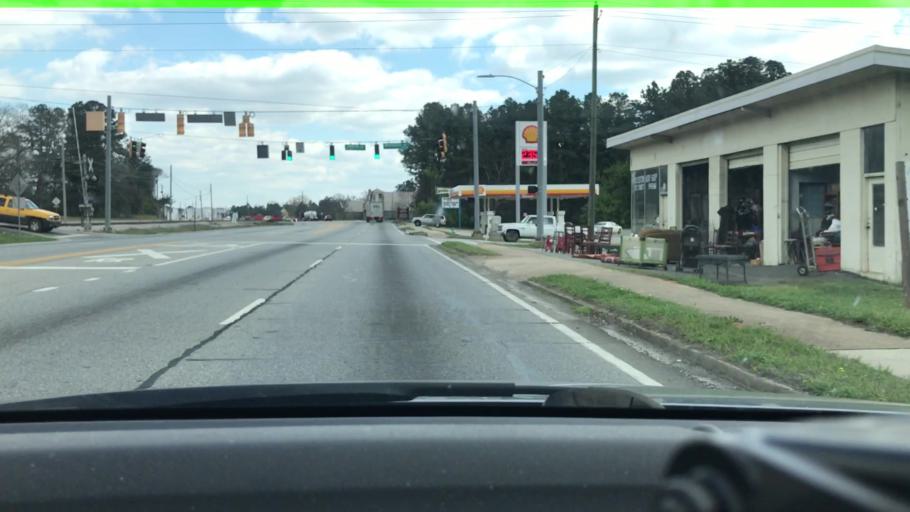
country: US
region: Georgia
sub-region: Clarke County
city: Country Club Estates
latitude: 33.9903
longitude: -83.4304
